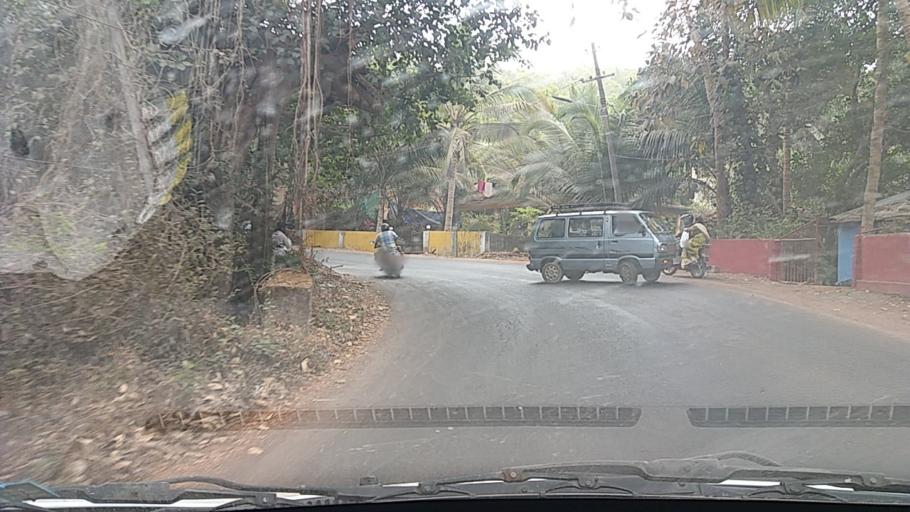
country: IN
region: Goa
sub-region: North Goa
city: Saligao
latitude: 15.5385
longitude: 73.7905
